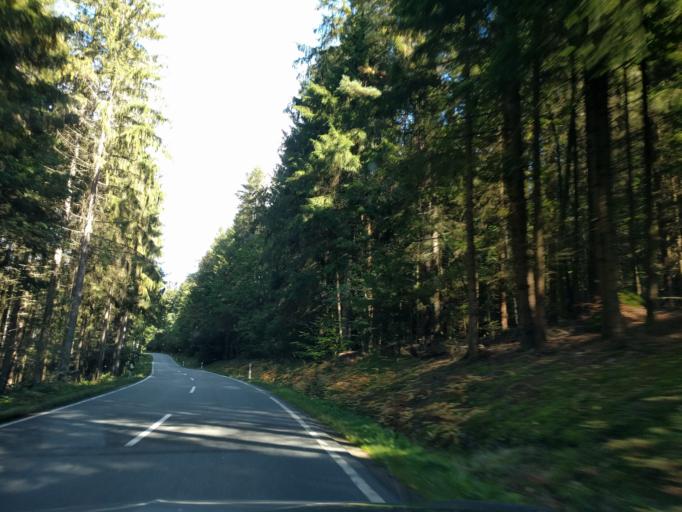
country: DE
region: Bavaria
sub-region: Lower Bavaria
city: Viechtach
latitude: 49.1121
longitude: 12.8861
